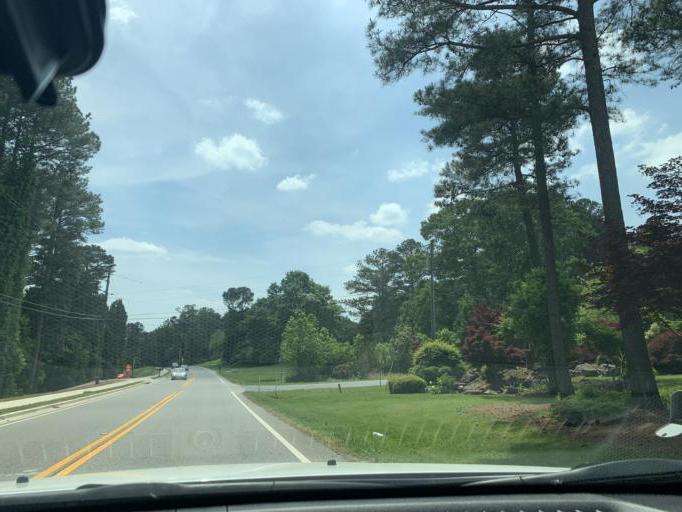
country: US
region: Georgia
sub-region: Forsyth County
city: Cumming
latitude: 34.1370
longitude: -84.1492
